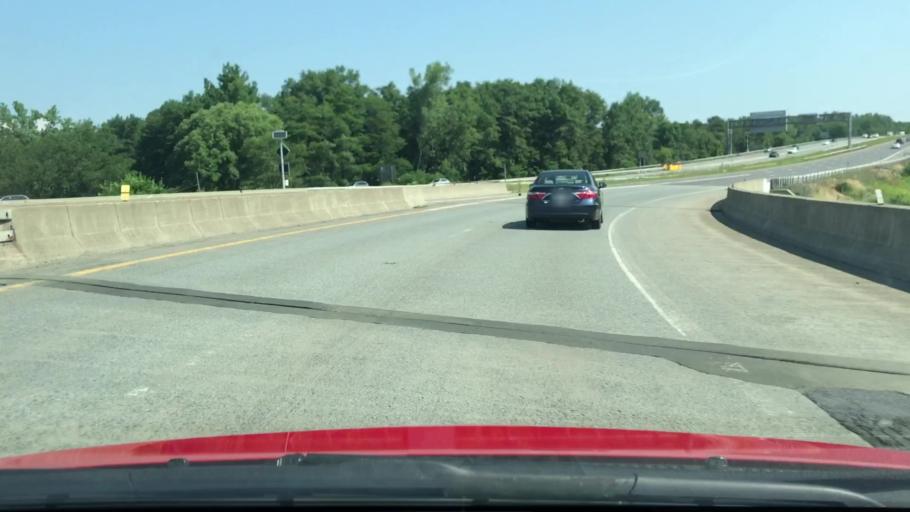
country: US
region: New York
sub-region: Albany County
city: McKownville
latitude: 42.6978
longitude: -73.8366
